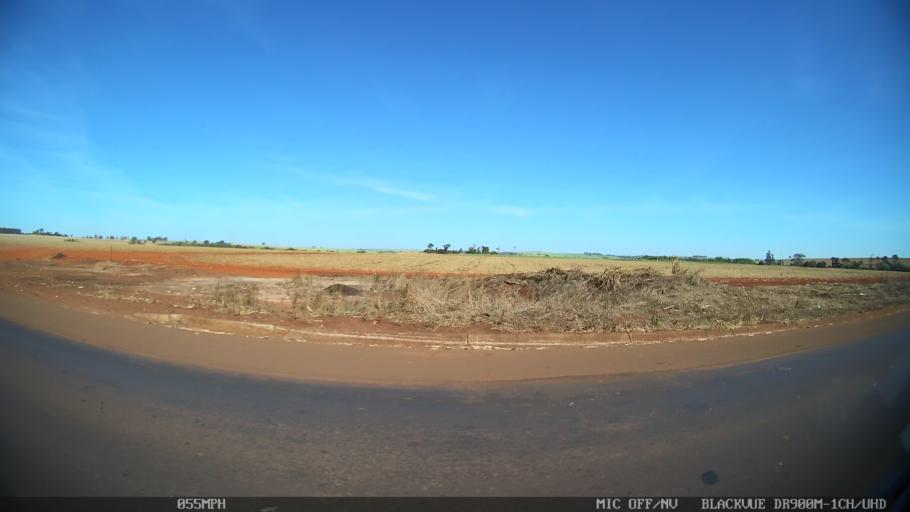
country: BR
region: Sao Paulo
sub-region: Sao Joaquim Da Barra
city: Sao Joaquim da Barra
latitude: -20.5146
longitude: -47.8907
